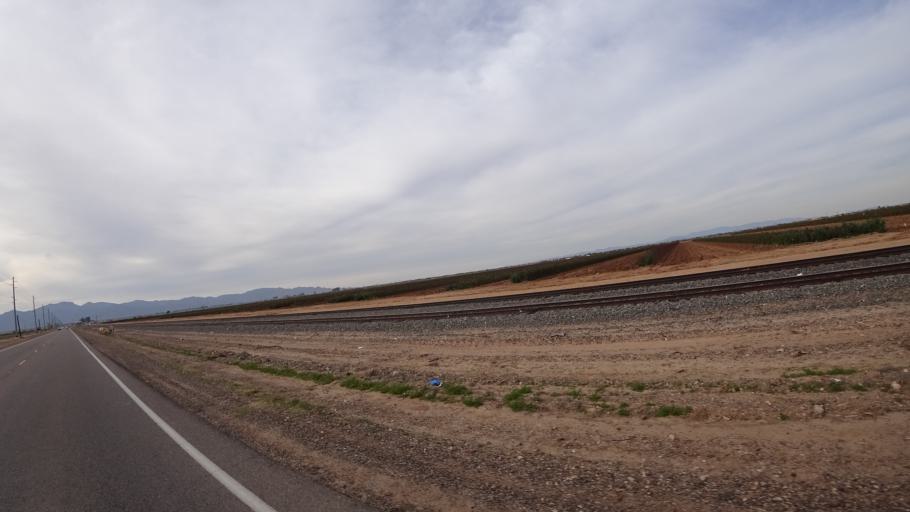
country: US
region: Arizona
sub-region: Maricopa County
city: Citrus Park
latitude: 33.5660
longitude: -112.3863
